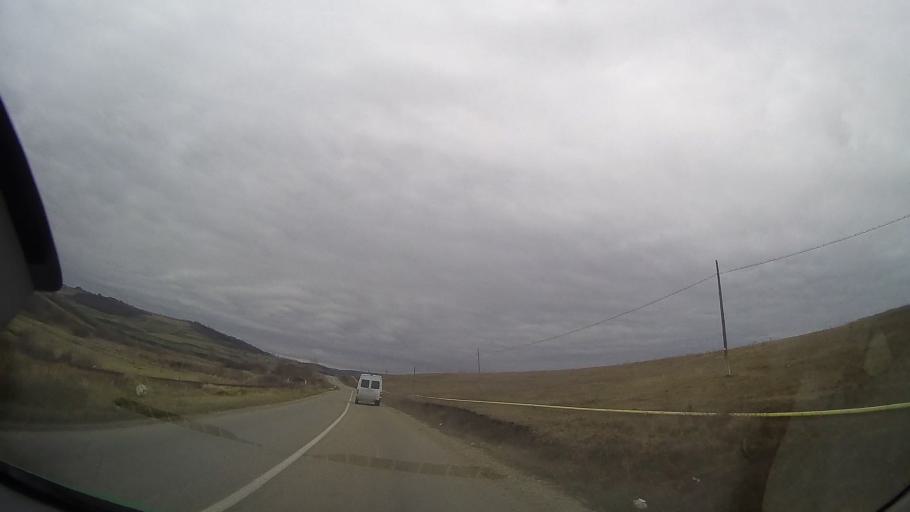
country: RO
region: Cluj
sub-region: Comuna Catina
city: Catina
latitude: 46.8041
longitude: 24.2143
